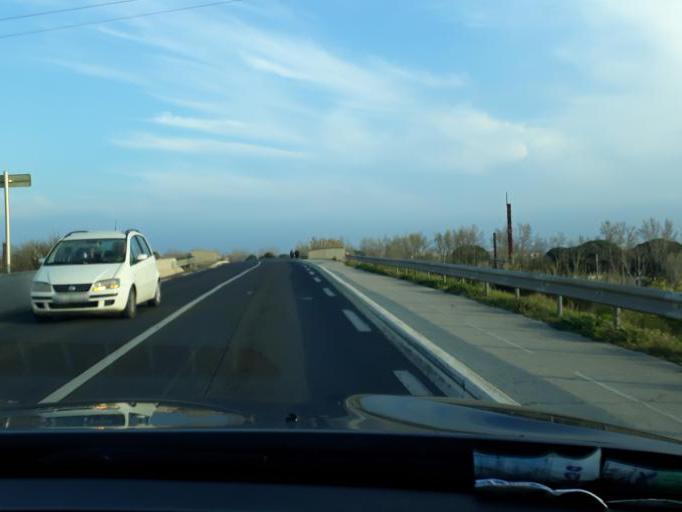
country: FR
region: Languedoc-Roussillon
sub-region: Departement de l'Herault
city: Marseillan
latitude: 43.3207
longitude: 3.5392
